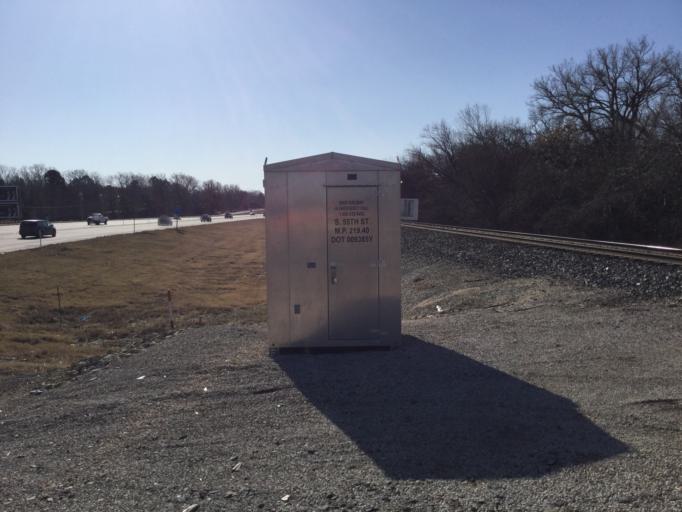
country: US
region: Kansas
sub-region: Sedgwick County
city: Derby
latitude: 37.5915
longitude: -97.2852
